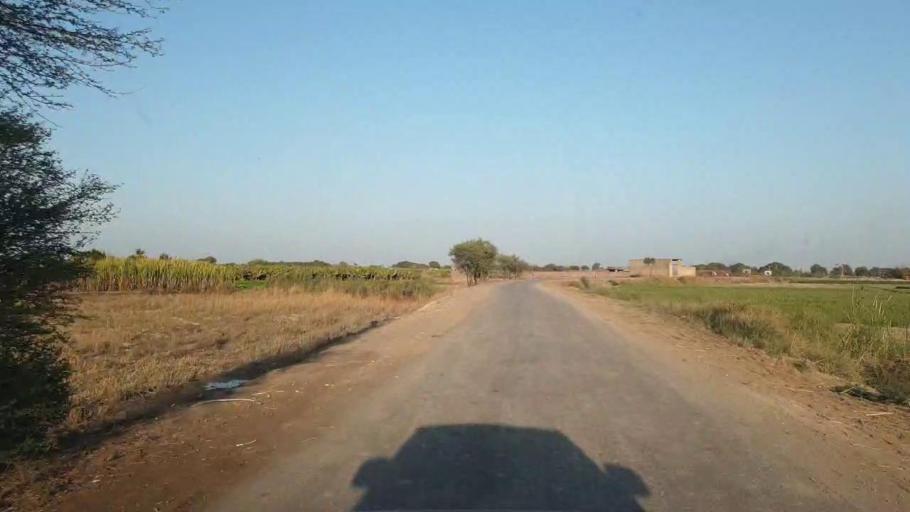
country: PK
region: Sindh
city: Tando Allahyar
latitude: 25.3539
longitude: 68.7135
